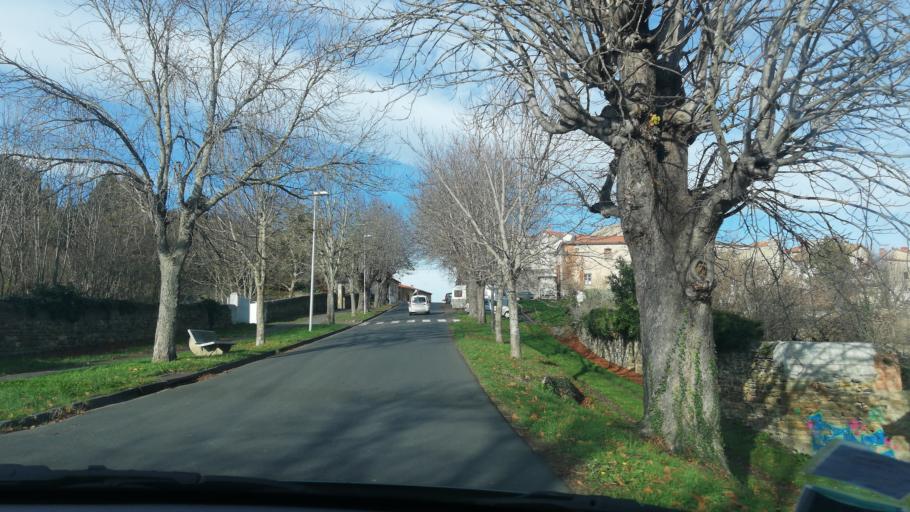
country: FR
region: Auvergne
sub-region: Departement du Puy-de-Dome
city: Billom
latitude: 45.7205
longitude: 3.3378
